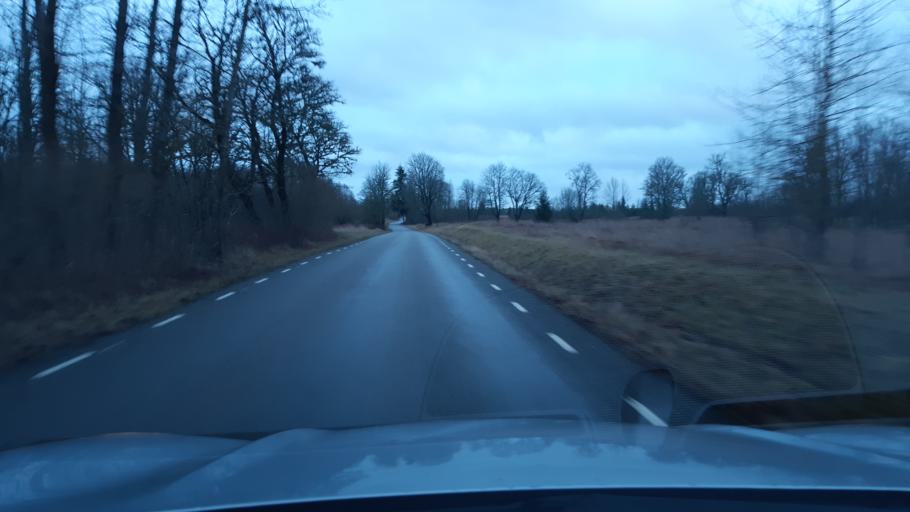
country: EE
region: Raplamaa
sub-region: Rapla vald
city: Rapla
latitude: 58.9949
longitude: 24.7209
